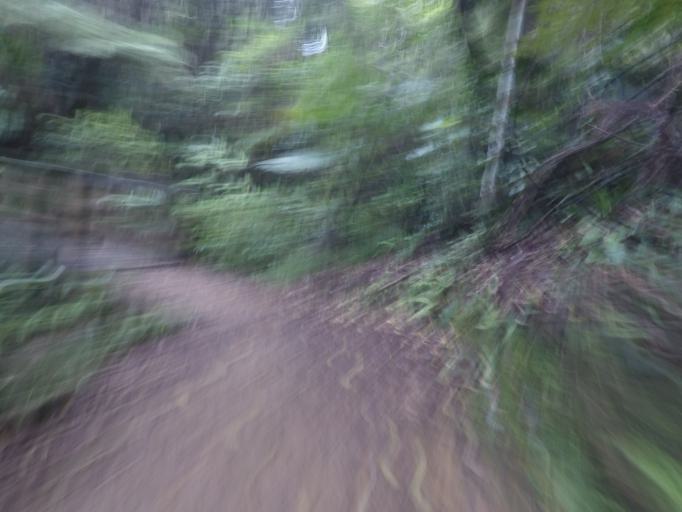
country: NZ
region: Bay of Plenty
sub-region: Western Bay of Plenty District
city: Waihi Beach
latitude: -37.3896
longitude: 175.9382
